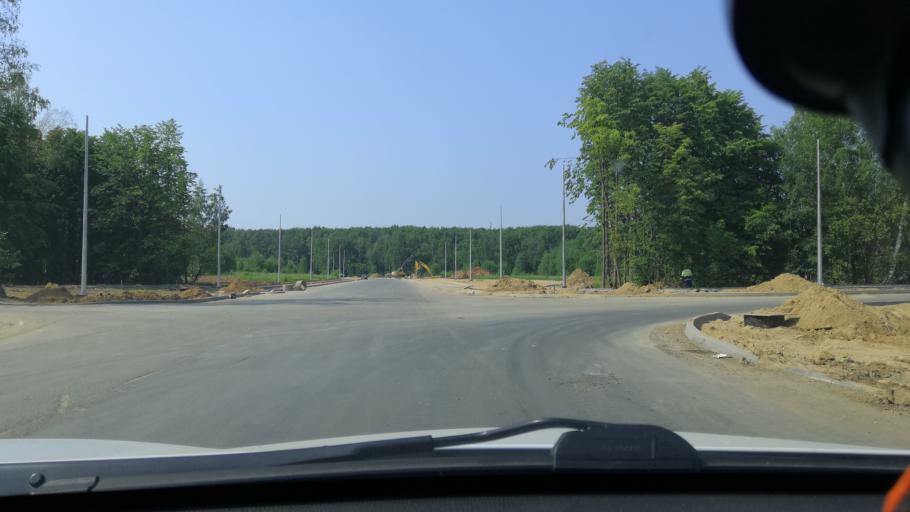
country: RU
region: Moscow
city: Severnyy
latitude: 55.9378
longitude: 37.5297
